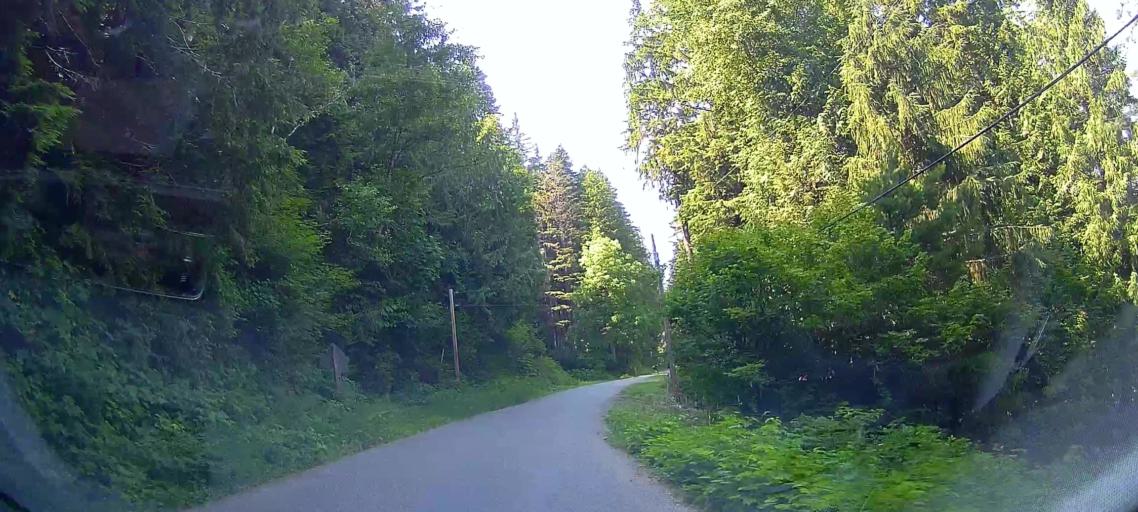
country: US
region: Washington
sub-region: Snohomish County
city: Arlington Heights
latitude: 48.3126
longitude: -121.9976
